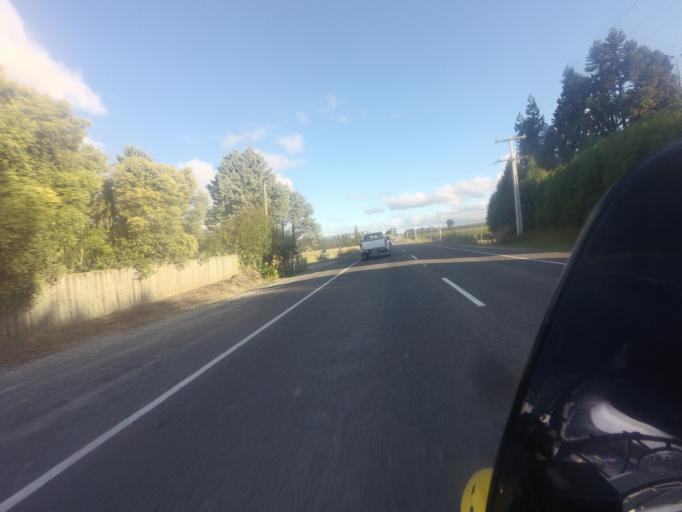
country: NZ
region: Gisborne
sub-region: Gisborne District
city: Gisborne
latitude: -38.5614
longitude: 177.9237
